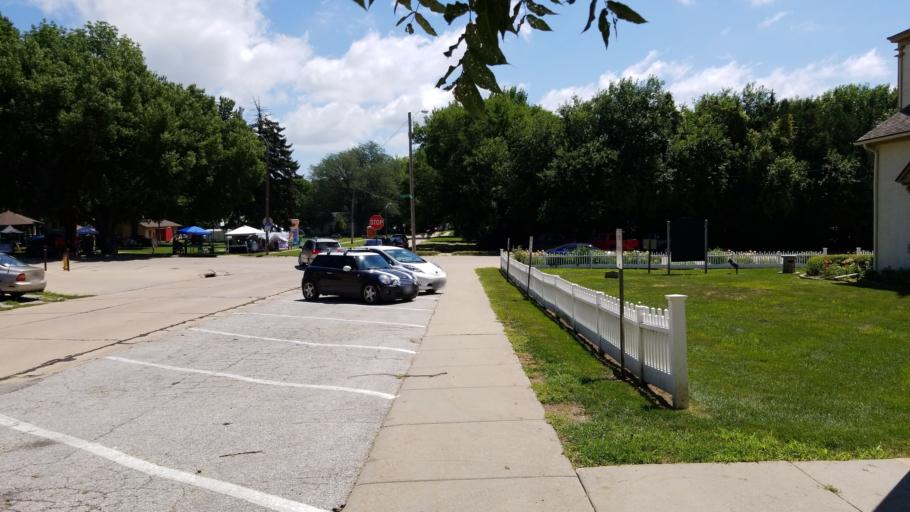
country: US
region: Nebraska
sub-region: Sarpy County
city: Bellevue
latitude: 41.1395
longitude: -95.8943
